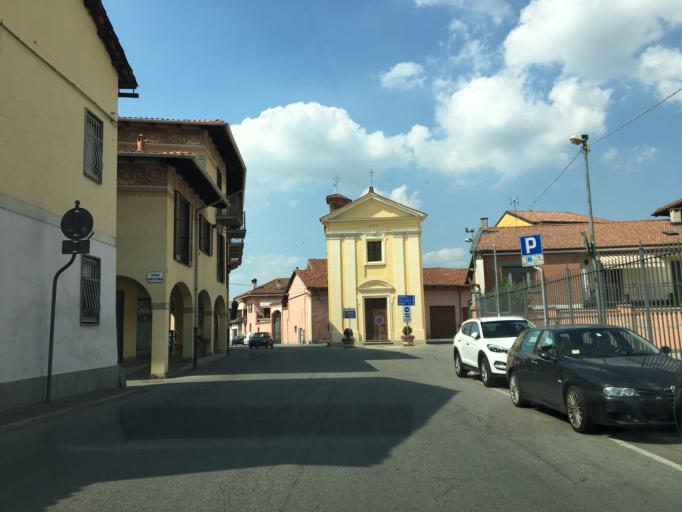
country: IT
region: Piedmont
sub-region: Provincia di Cuneo
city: Caramagna Piemonte
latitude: 44.7811
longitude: 7.7391
